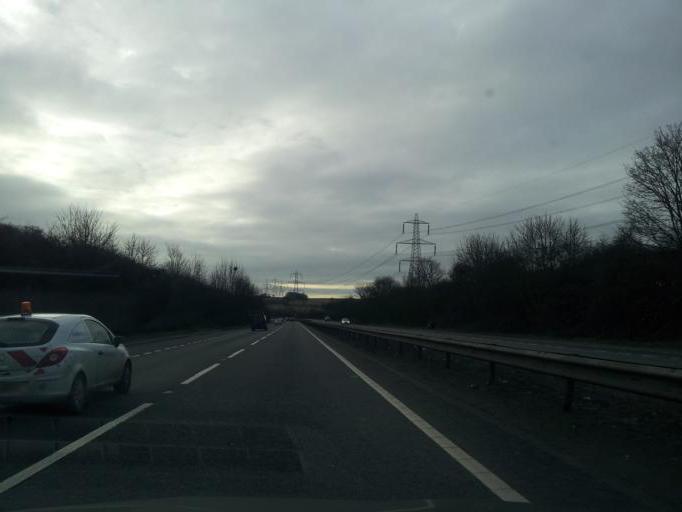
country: GB
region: England
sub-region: Lincolnshire
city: Barrowby
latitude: 52.9035
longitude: -0.6708
